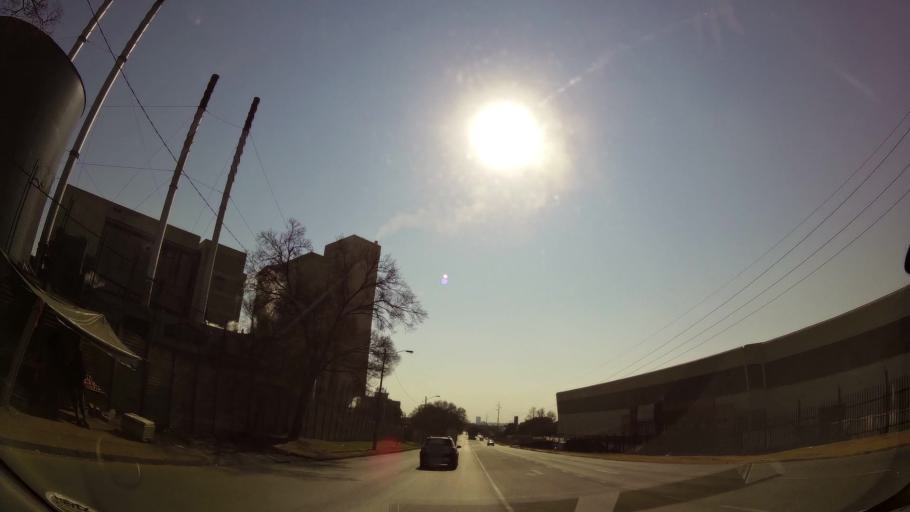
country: ZA
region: Gauteng
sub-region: City of Johannesburg Metropolitan Municipality
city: Modderfontein
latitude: -26.1359
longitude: 28.2153
